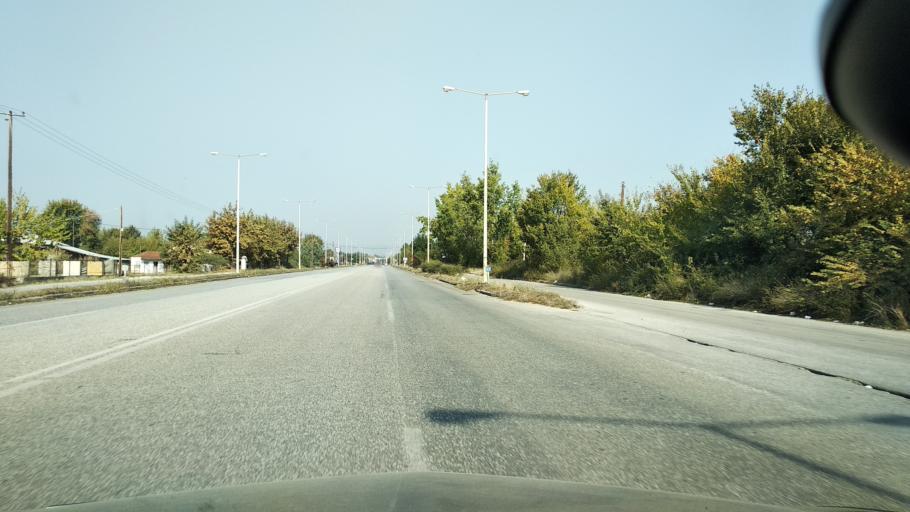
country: GR
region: Thessaly
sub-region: Trikala
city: Pyrgetos
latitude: 39.5782
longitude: 21.7434
